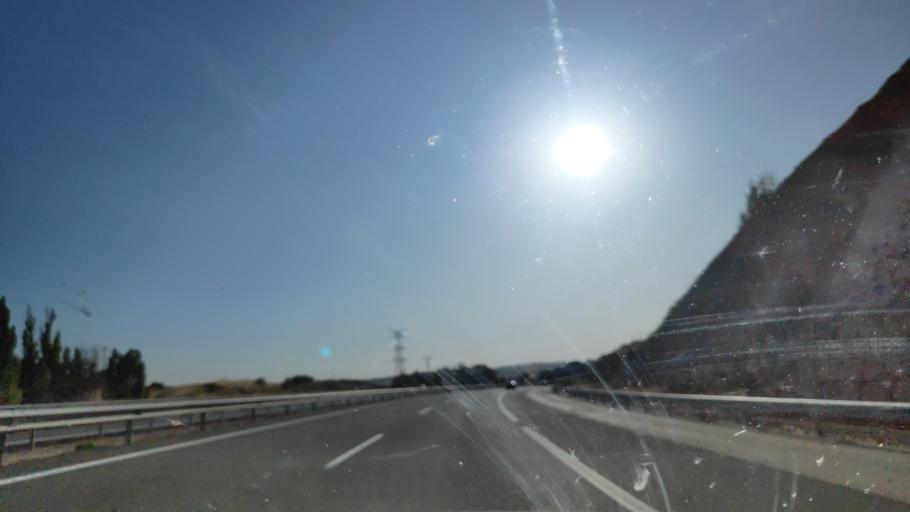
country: ES
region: Castille-La Mancha
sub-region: Provincia de Cuenca
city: Zafra de Zancara
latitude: 39.8592
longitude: -2.5403
